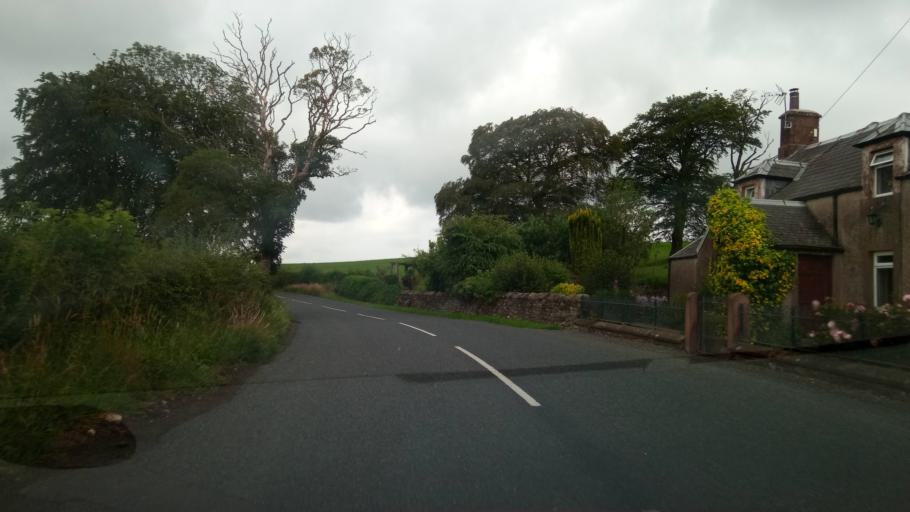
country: GB
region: Scotland
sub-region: Dumfries and Galloway
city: Langholm
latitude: 55.0948
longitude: -2.9001
